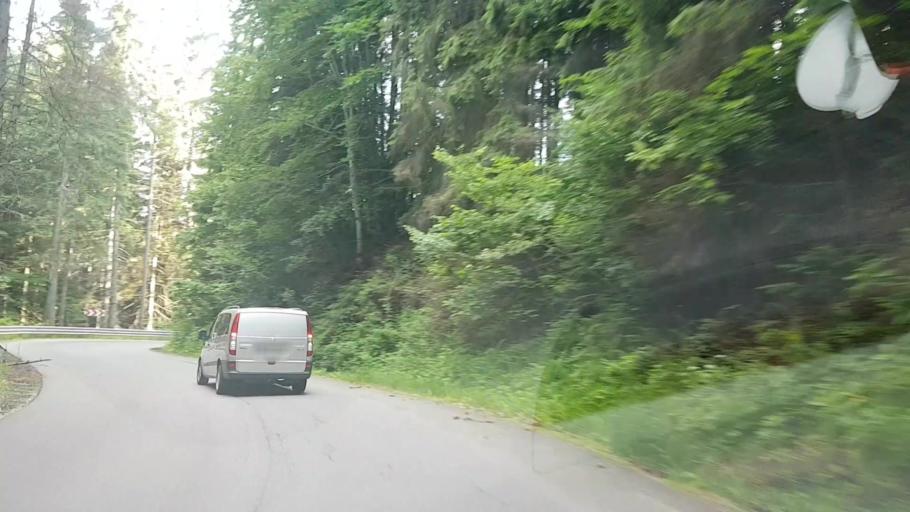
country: RO
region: Harghita
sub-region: Comuna Varsag
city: Varsag
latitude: 46.6696
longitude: 25.3320
